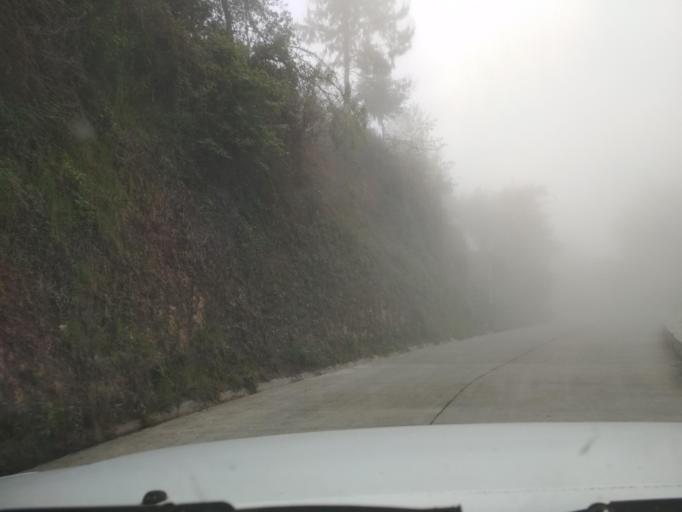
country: MX
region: Veracruz
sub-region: La Perla
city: Chilapa
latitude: 18.9779
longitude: -97.1906
